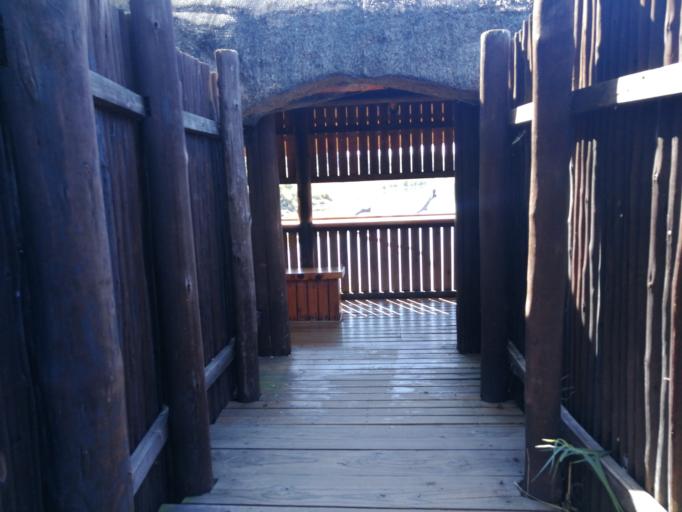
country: ZA
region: Limpopo
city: Thulamahashi
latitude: -24.9814
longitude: 31.5661
